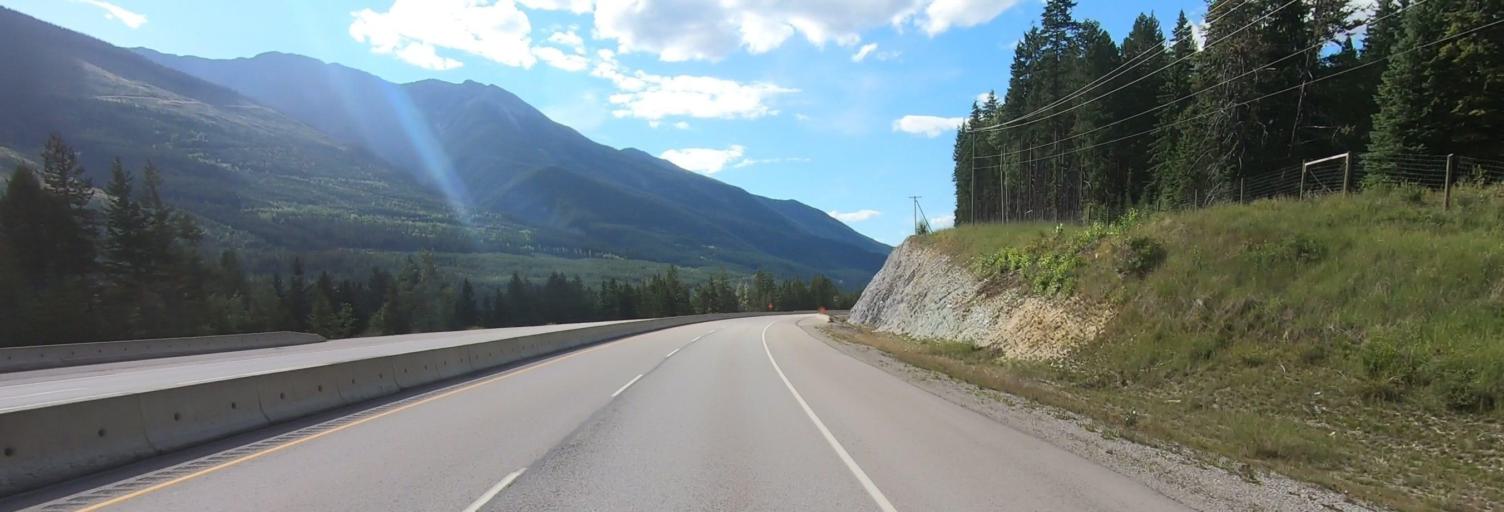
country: CA
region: British Columbia
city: Golden
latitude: 51.2606
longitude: -116.7260
